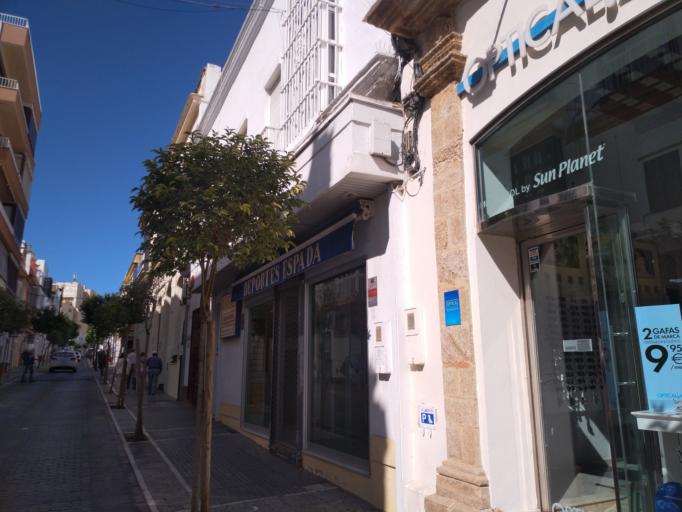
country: ES
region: Andalusia
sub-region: Provincia de Cadiz
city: San Fernando
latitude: 36.4683
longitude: -6.1956
